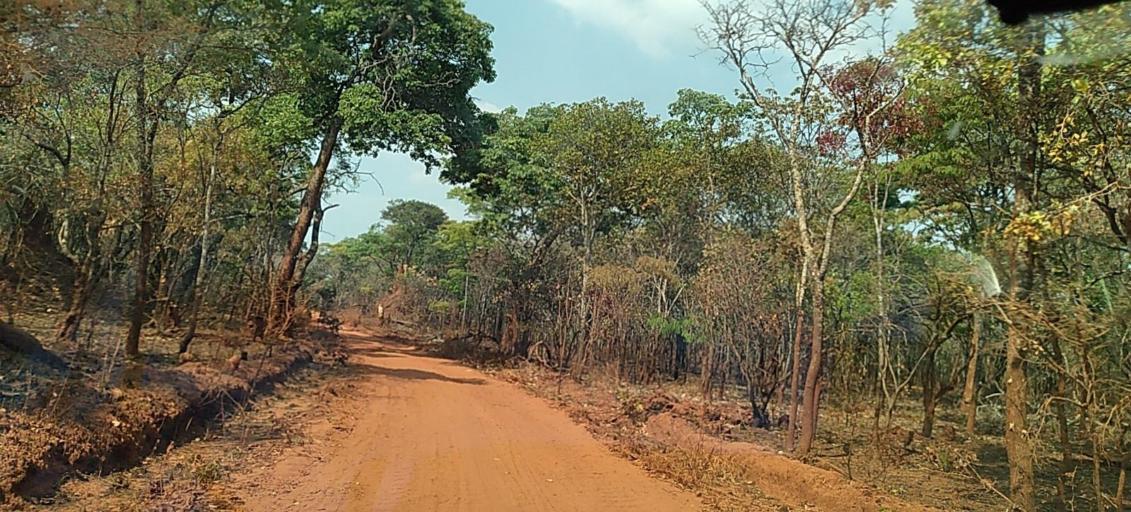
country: ZM
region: North-Western
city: Kasempa
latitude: -13.3169
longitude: 26.0560
